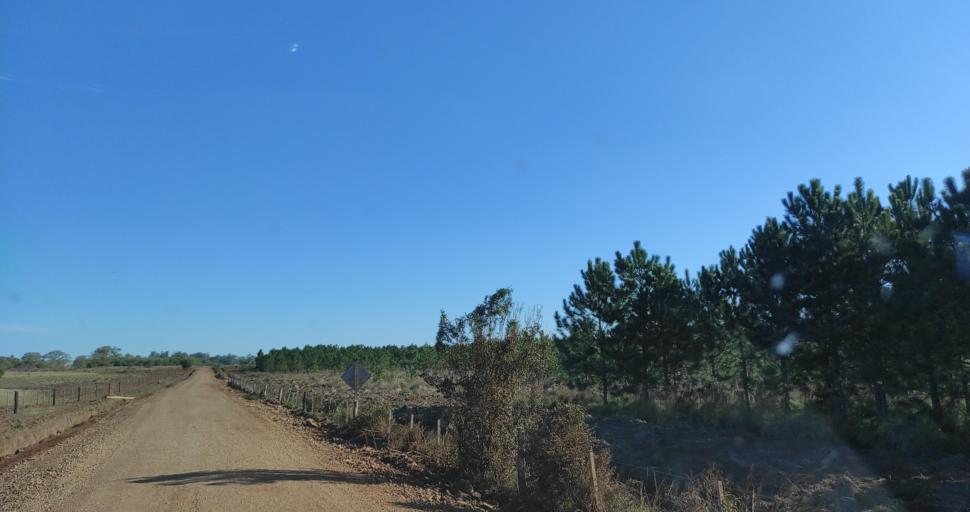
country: PY
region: Itapua
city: San Juan del Parana
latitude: -27.4241
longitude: -56.0984
